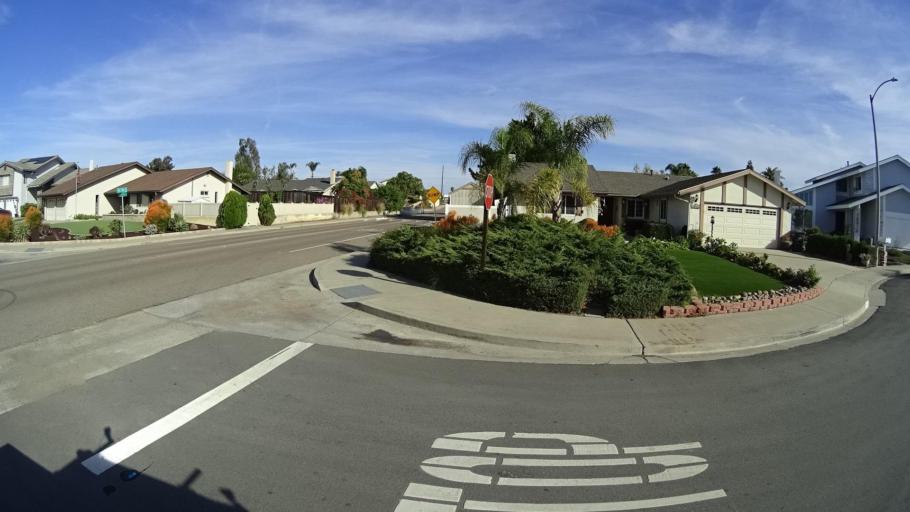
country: US
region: California
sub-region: San Diego County
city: Casa de Oro-Mount Helix
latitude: 32.7381
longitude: -116.9609
